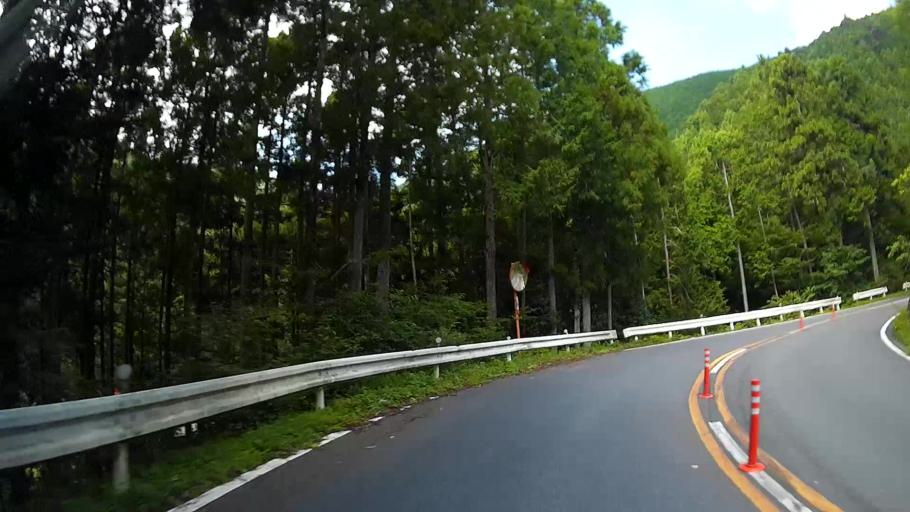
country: JP
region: Saitama
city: Chichibu
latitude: 35.9266
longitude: 139.1491
